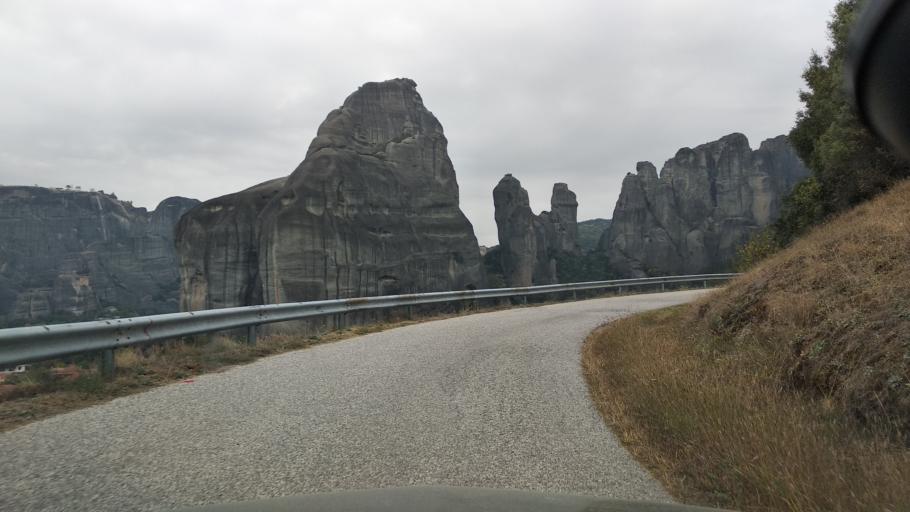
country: GR
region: Thessaly
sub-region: Trikala
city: Kastraki
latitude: 39.7148
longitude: 21.6192
